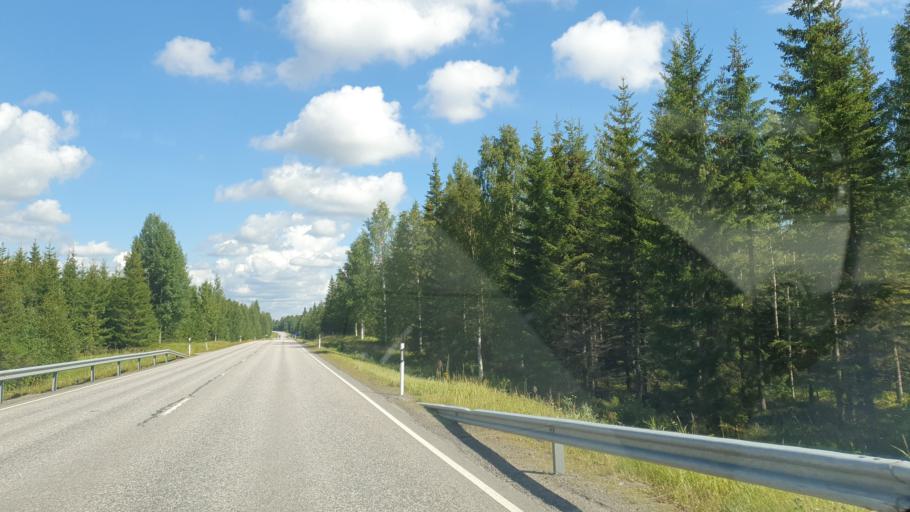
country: FI
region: Northern Savo
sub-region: Ylae-Savo
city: Sonkajaervi
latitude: 63.6887
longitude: 27.3447
